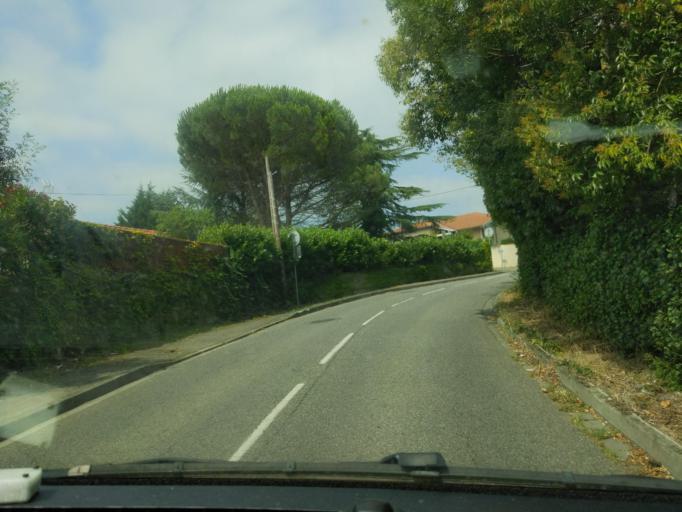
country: FR
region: Midi-Pyrenees
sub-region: Departement de la Haute-Garonne
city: Saint-Orens-de-Gameville
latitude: 43.5458
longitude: 1.5334
